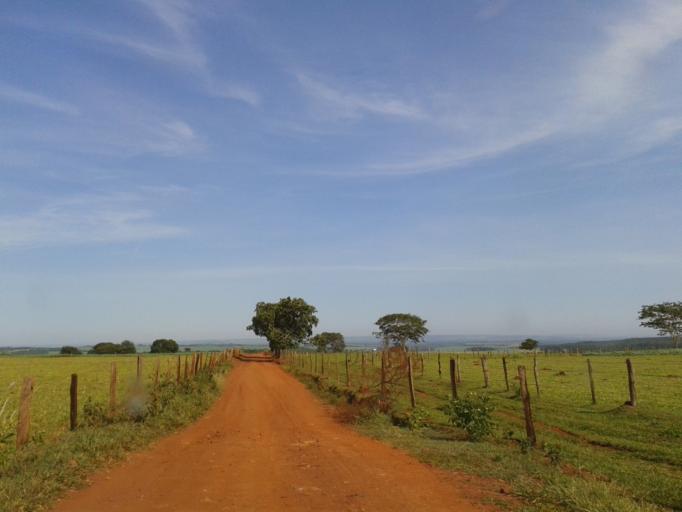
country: BR
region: Minas Gerais
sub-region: Centralina
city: Centralina
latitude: -18.7131
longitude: -49.2019
